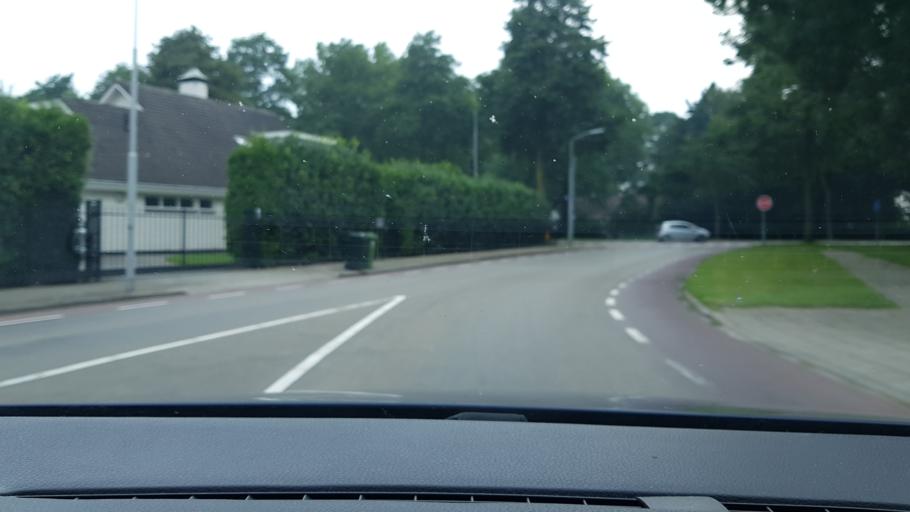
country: NL
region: Gelderland
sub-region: Gemeente Beuningen
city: Beuningen
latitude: 51.8623
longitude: 5.7812
